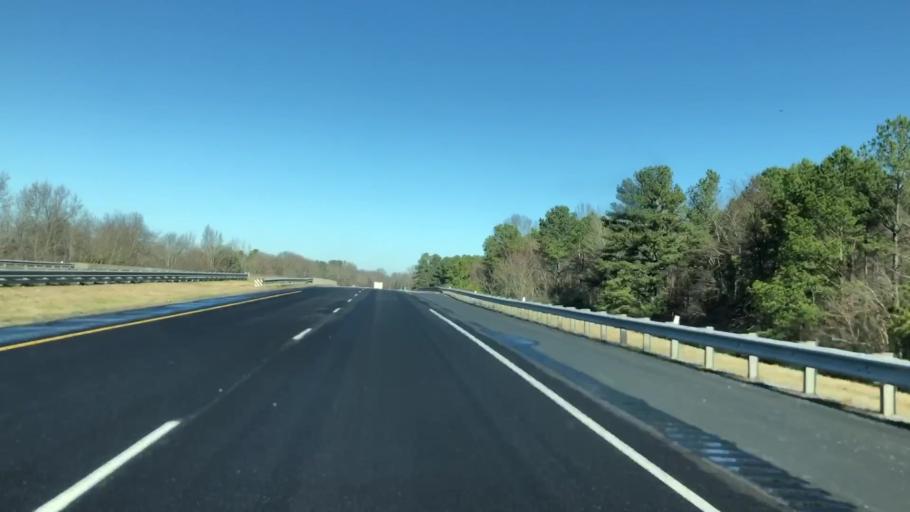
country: US
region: Alabama
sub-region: Limestone County
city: Ardmore
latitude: 34.9054
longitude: -86.9063
